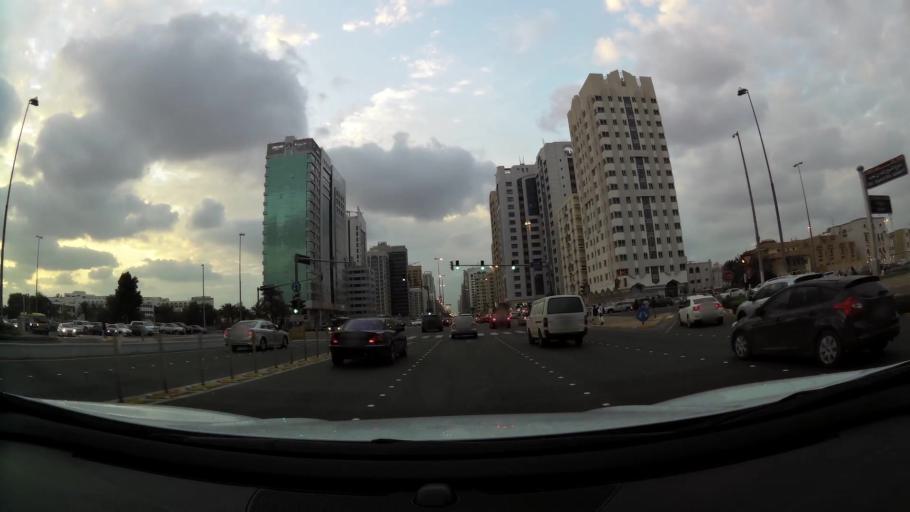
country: AE
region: Abu Dhabi
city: Abu Dhabi
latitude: 24.4629
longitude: 54.3778
